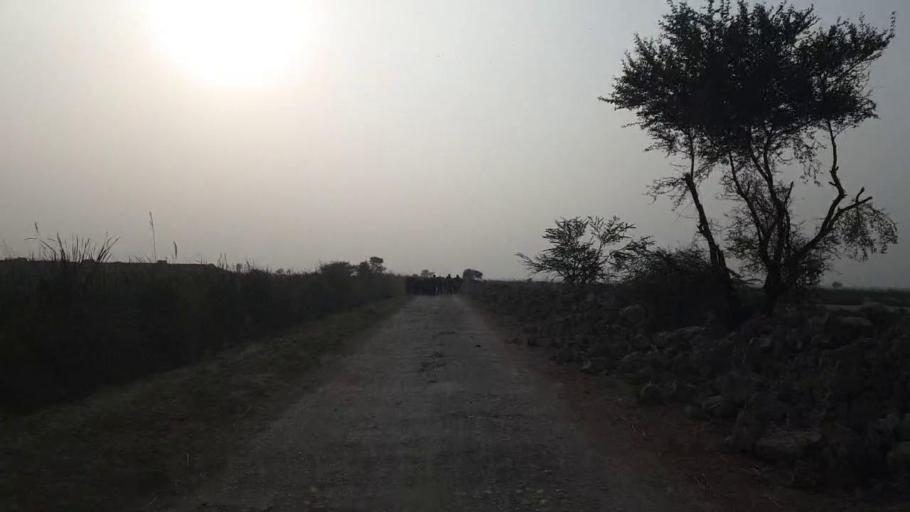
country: PK
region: Sindh
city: Mirpur Batoro
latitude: 24.6544
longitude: 68.3808
